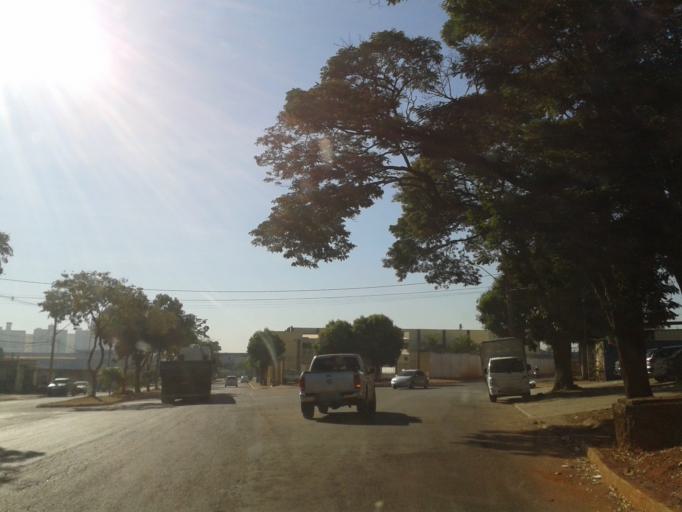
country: BR
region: Goias
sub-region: Goiania
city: Goiania
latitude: -16.6521
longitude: -49.3353
